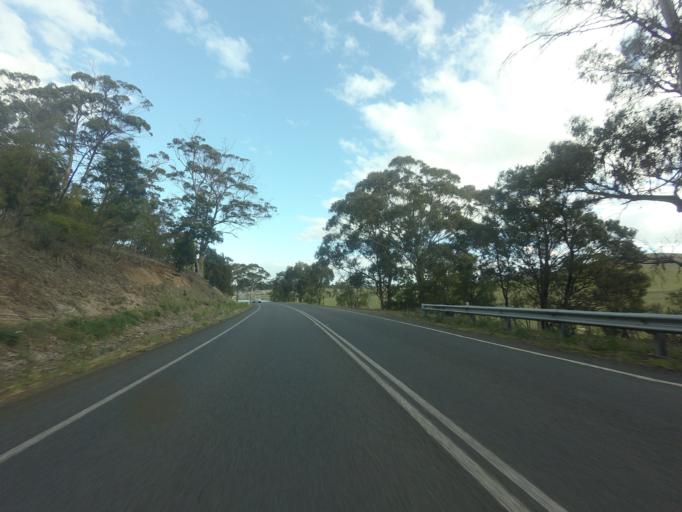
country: AU
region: Tasmania
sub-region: Sorell
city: Sorell
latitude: -42.7095
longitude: 147.5104
